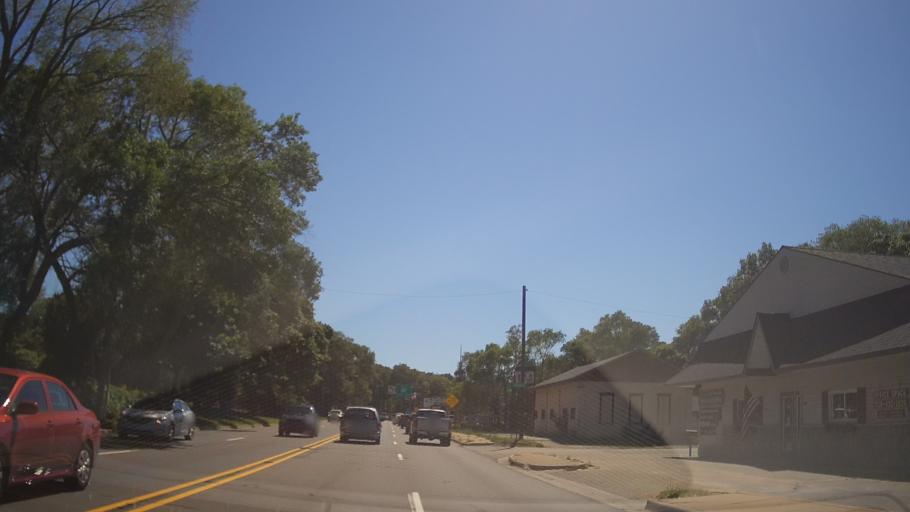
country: US
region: Michigan
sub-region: Emmet County
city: Petoskey
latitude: 45.3880
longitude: -84.9219
